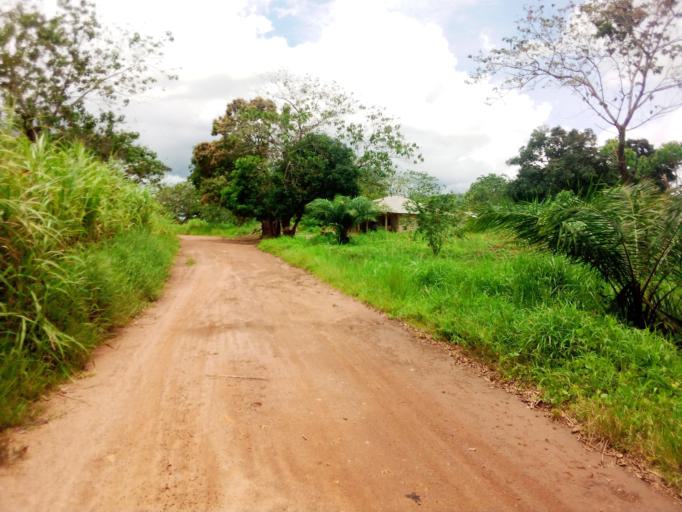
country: SL
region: Eastern Province
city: Simbakoro
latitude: 8.6064
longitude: -10.9851
